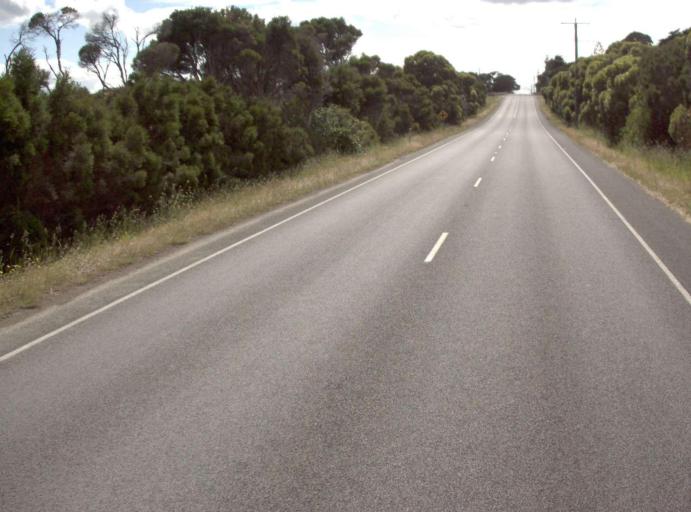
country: AU
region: Victoria
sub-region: Bass Coast
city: Phillip Island
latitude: -38.4967
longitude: 145.1985
